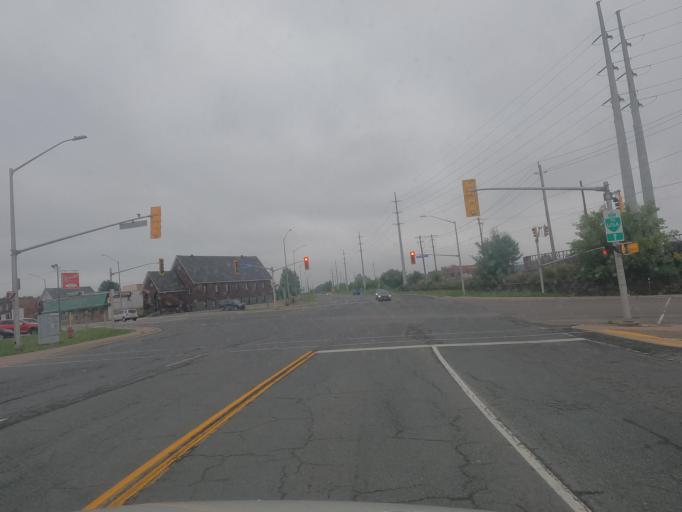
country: CA
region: Ontario
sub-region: Algoma
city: Sault Ste. Marie
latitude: 46.5272
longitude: -84.3481
